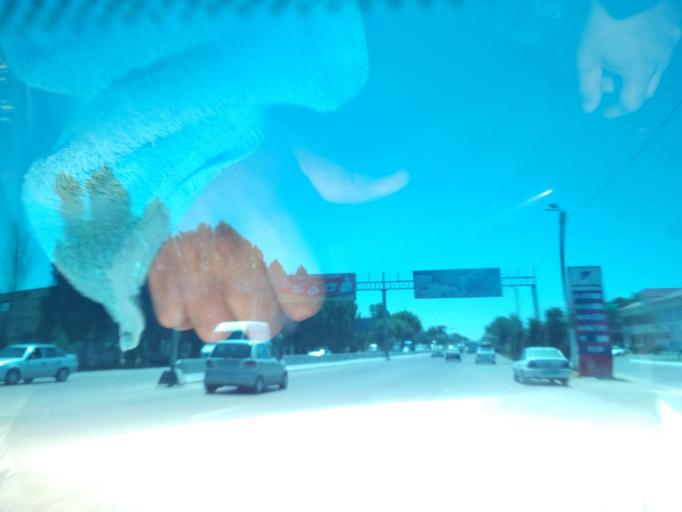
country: UZ
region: Toshkent
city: Urtaowul
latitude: 41.2300
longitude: 69.1512
